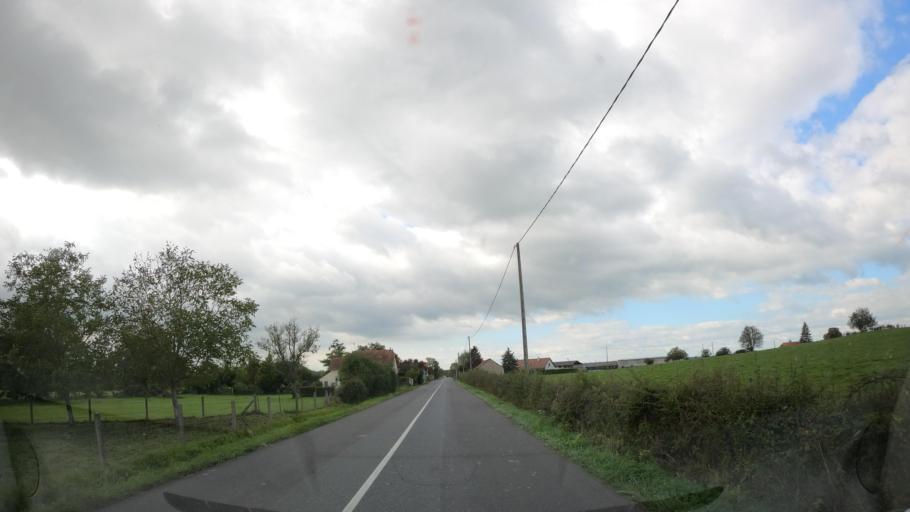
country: FR
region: Auvergne
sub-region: Departement de l'Allier
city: Lapalisse
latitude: 46.3678
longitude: 3.6212
